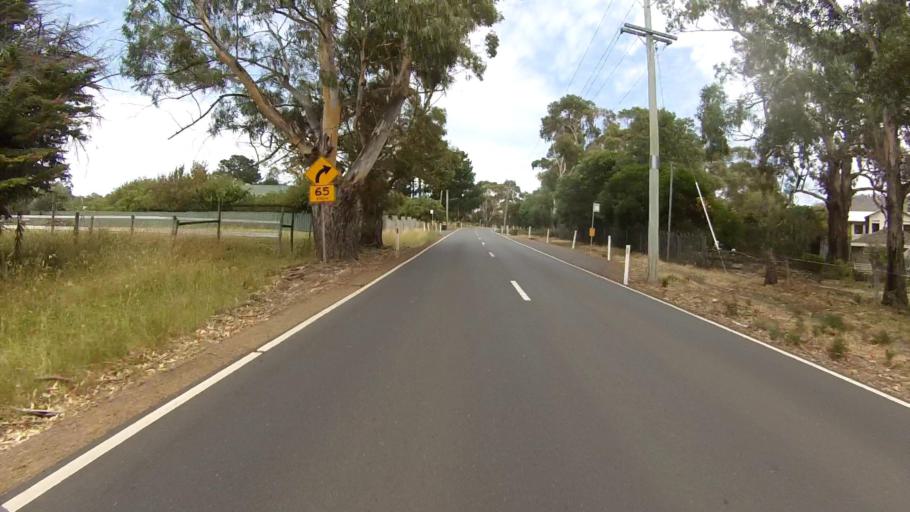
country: AU
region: Tasmania
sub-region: Clarence
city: Acton Park
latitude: -42.8664
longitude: 147.4883
